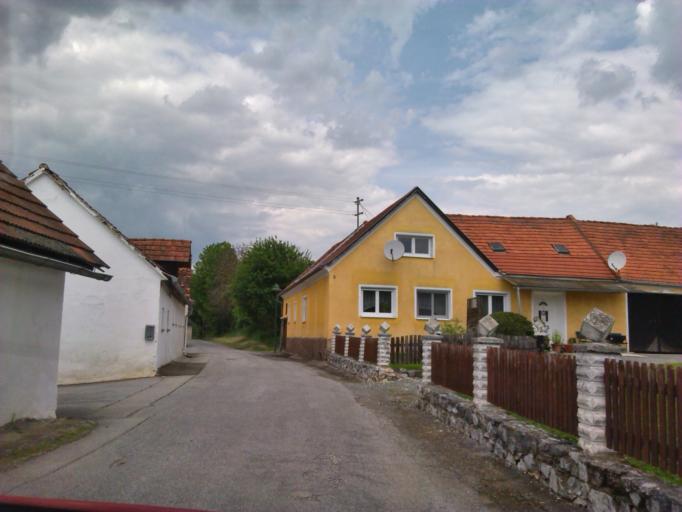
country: AT
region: Styria
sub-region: Politischer Bezirk Hartberg-Fuerstenfeld
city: Hainersdorf
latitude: 47.0993
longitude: 15.9727
